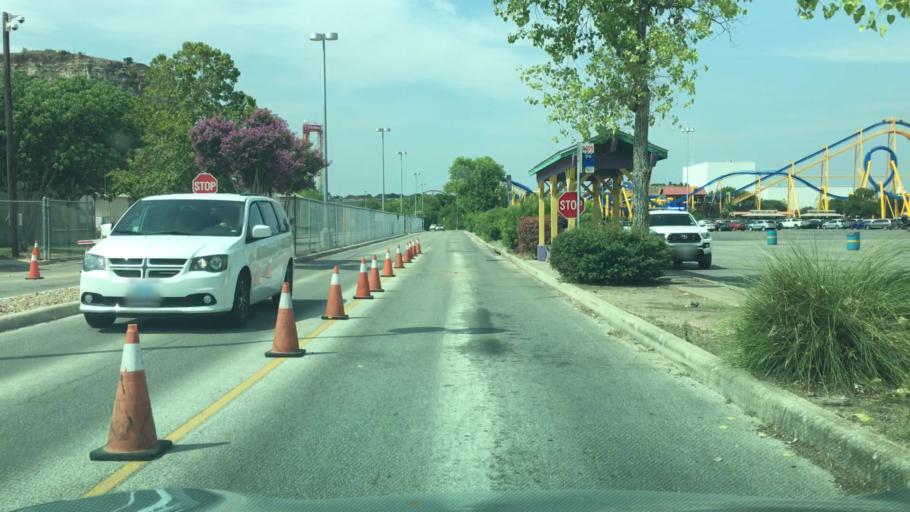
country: US
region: Texas
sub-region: Bexar County
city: Shavano Park
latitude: 29.6007
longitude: -98.6058
